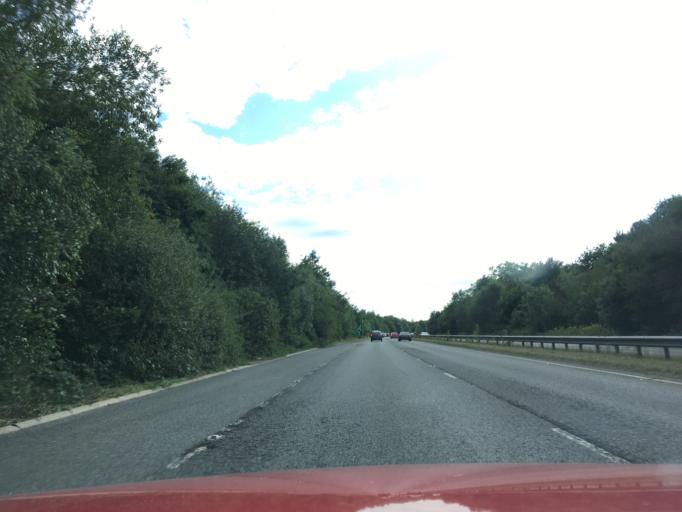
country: GB
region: England
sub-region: West Sussex
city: Horsham
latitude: 51.0827
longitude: -0.3348
